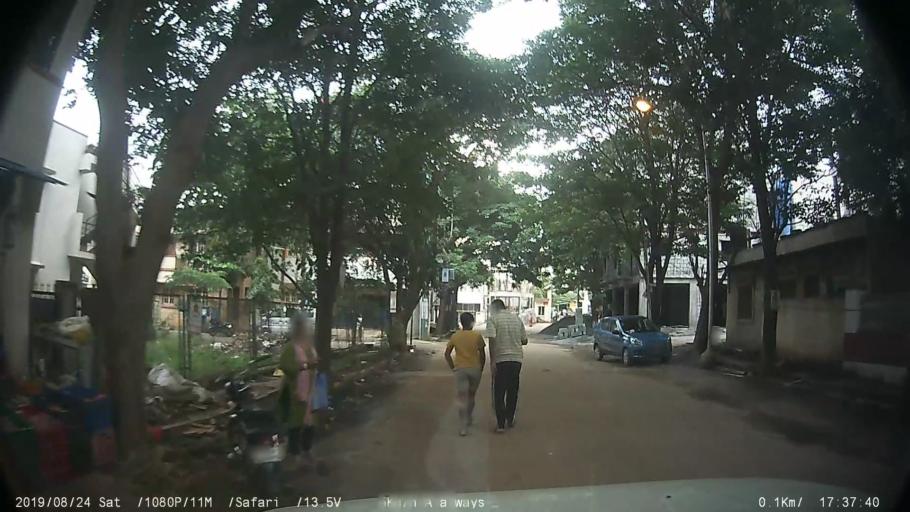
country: IN
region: Karnataka
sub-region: Bangalore Urban
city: Anekal
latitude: 12.8279
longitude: 77.6912
